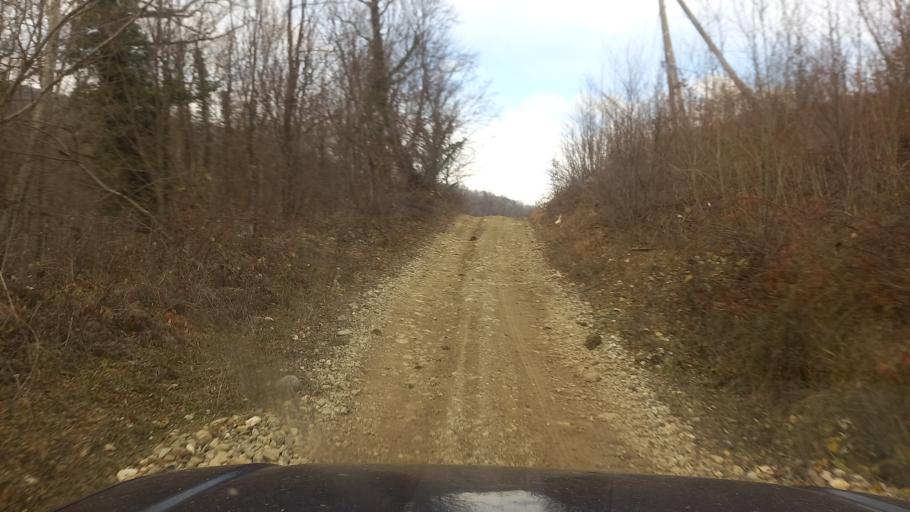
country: RU
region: Krasnodarskiy
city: Neftegorsk
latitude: 44.2124
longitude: 39.7115
